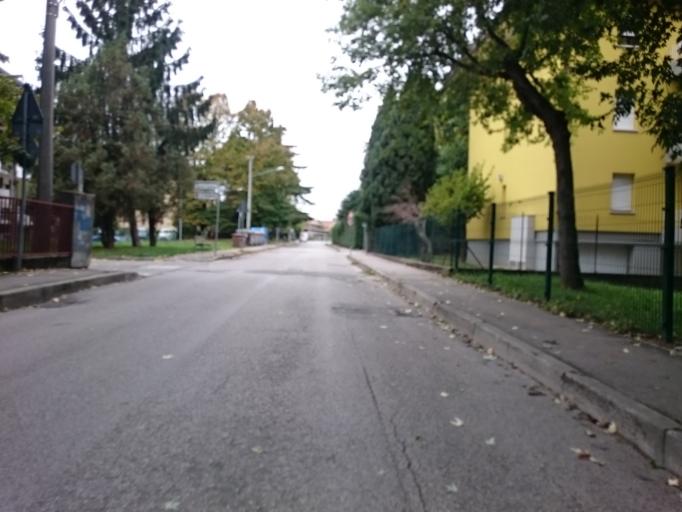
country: IT
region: Veneto
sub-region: Provincia di Padova
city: Caselle
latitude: 45.3942
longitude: 11.8325
